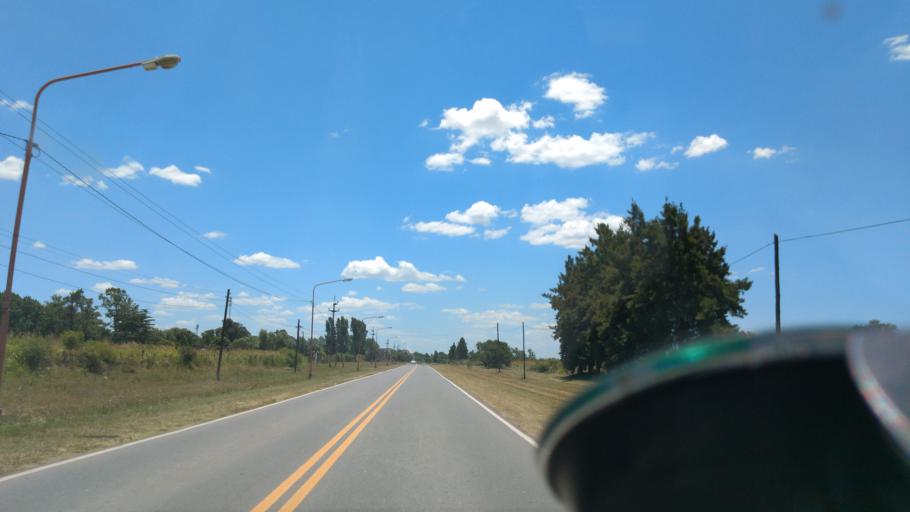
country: AR
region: Santa Fe
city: Laguna Paiva
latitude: -31.3250
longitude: -60.6591
